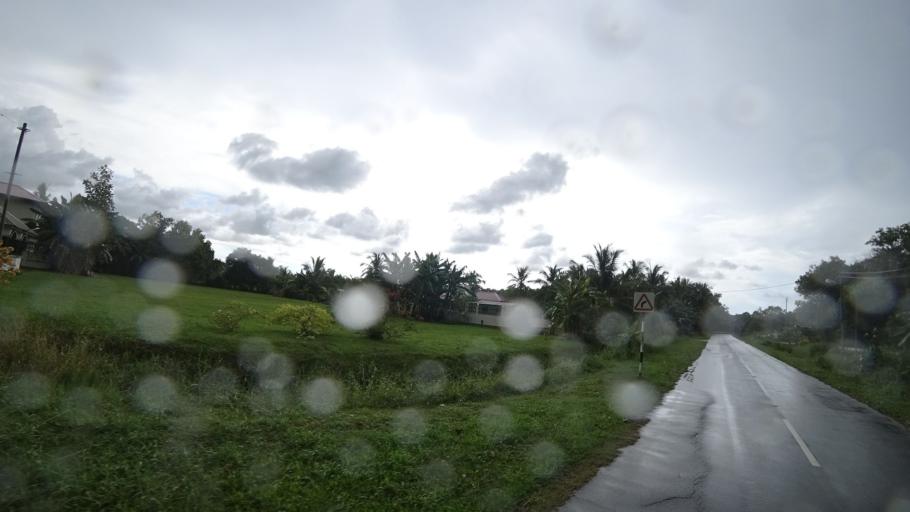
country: MY
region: Sarawak
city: Limbang
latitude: 4.8243
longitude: 114.9081
